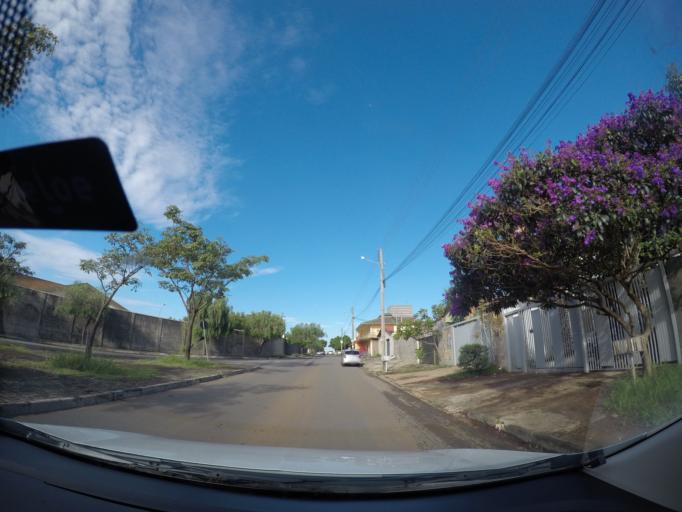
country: BR
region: Goias
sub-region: Aparecida De Goiania
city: Aparecida de Goiania
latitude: -16.7540
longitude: -49.2754
